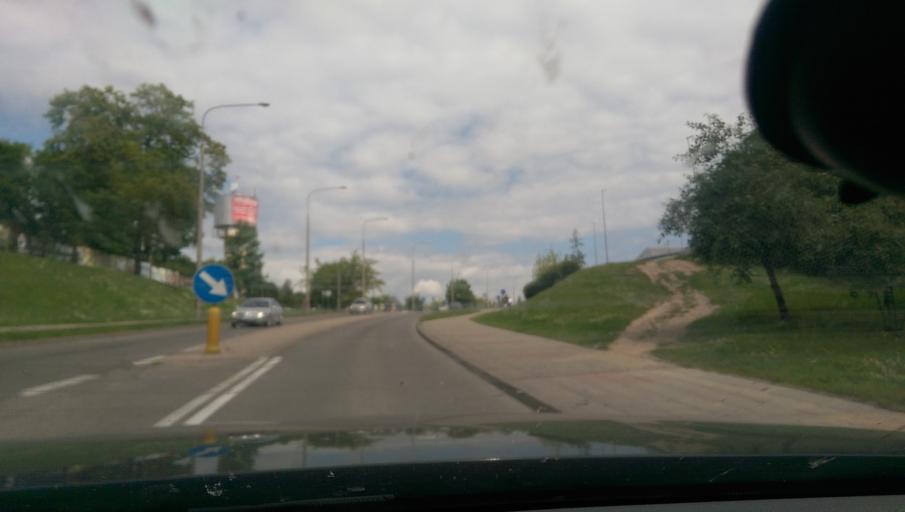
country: PL
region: Podlasie
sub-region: Suwalki
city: Suwalki
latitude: 54.1075
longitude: 22.9246
